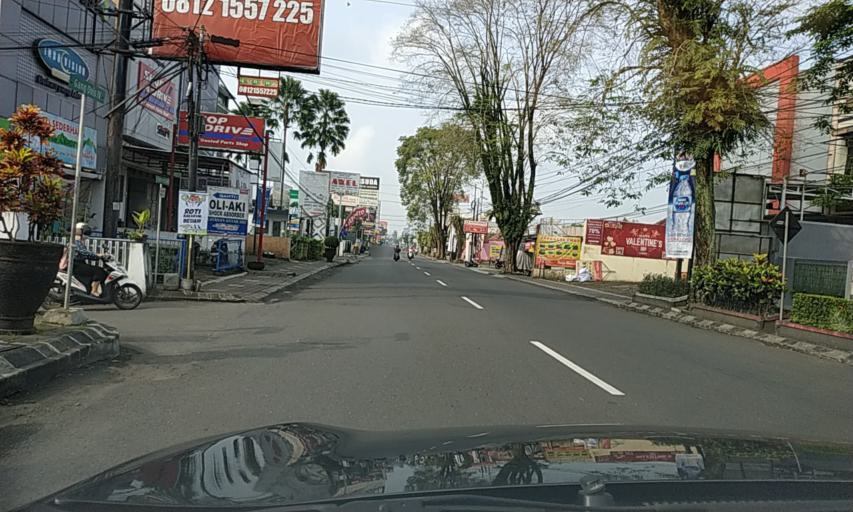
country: ID
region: Central Java
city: Purwokerto
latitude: -7.4183
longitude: 109.2446
